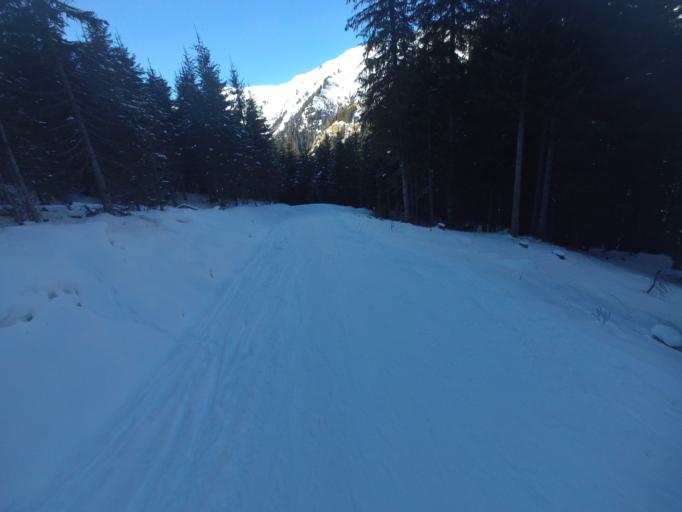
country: AT
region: Salzburg
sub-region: Politischer Bezirk Sankt Johann im Pongau
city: Huttschlag
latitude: 47.1839
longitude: 13.2816
